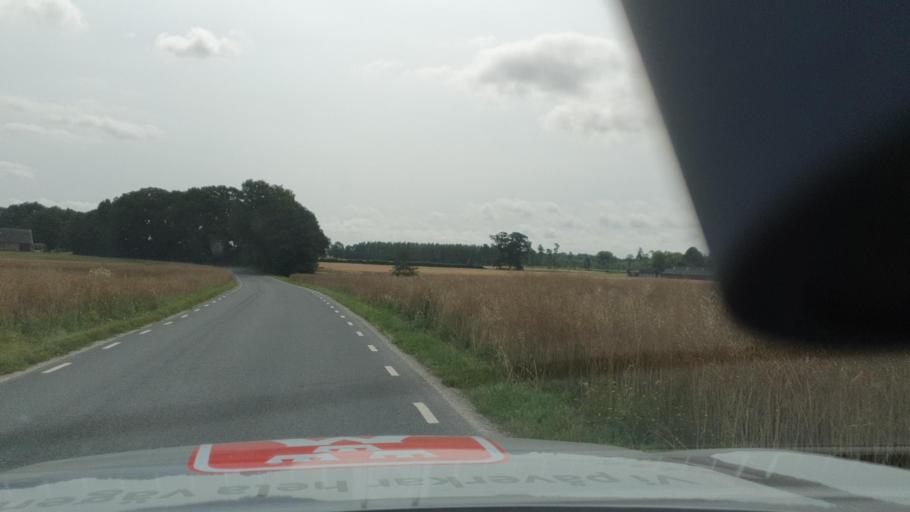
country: SE
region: Skane
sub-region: Kristianstads Kommun
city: Fjalkinge
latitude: 56.0548
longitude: 14.3755
